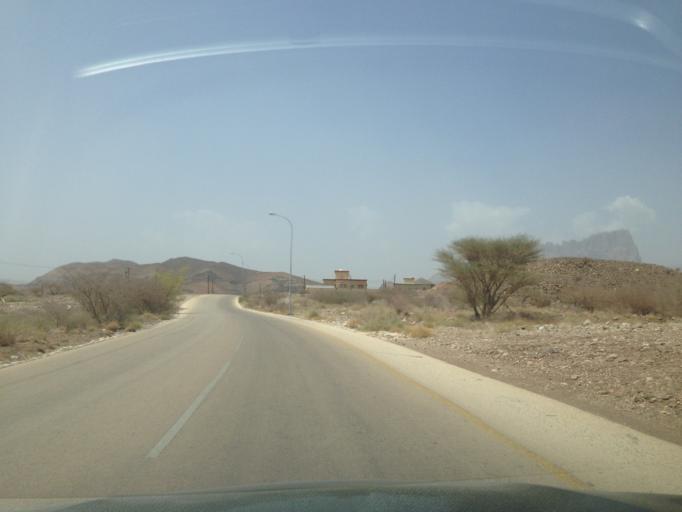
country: OM
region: Az Zahirah
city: `Ibri
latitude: 23.1810
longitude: 56.9202
